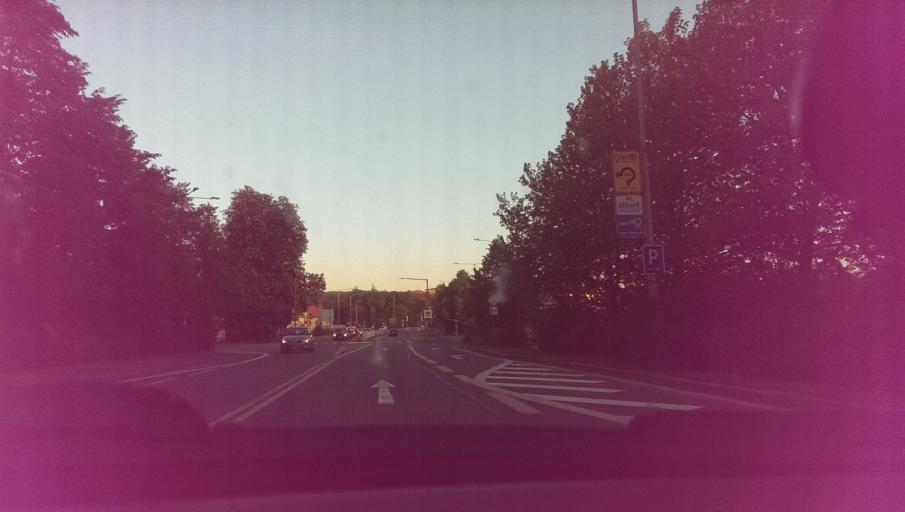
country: CZ
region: Zlin
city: Valasske Mezirici
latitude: 49.4761
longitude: 17.9707
